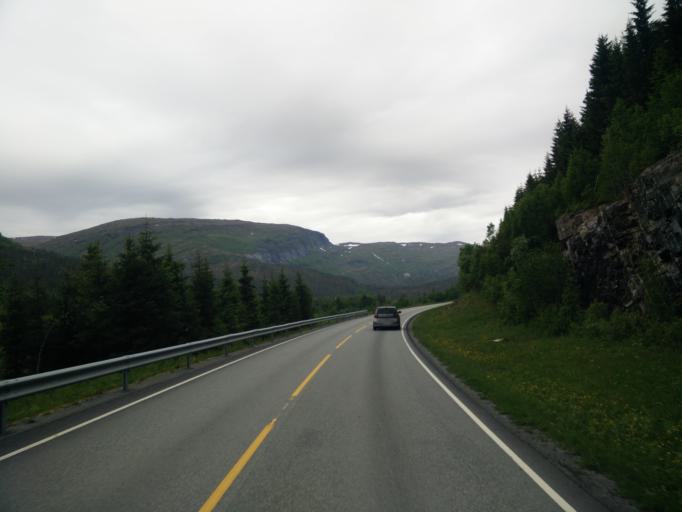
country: NO
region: Sor-Trondelag
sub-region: Hemne
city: Kyrksaeterora
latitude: 63.2104
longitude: 9.1808
